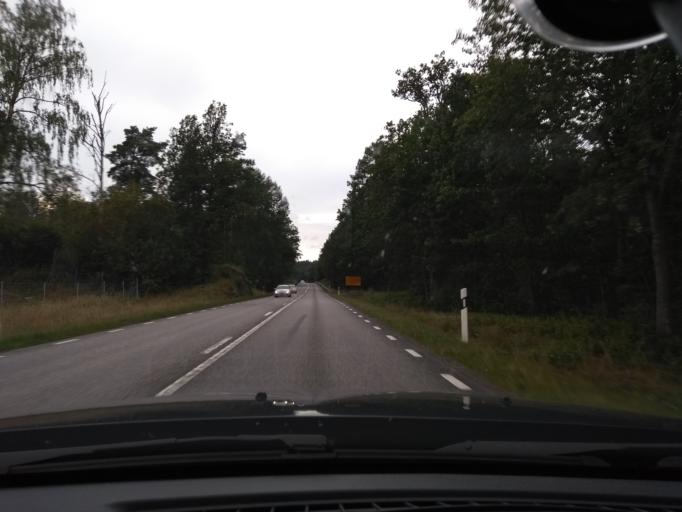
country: SE
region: Joenkoeping
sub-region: Eksjo Kommun
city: Eksjoe
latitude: 57.6342
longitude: 14.8892
